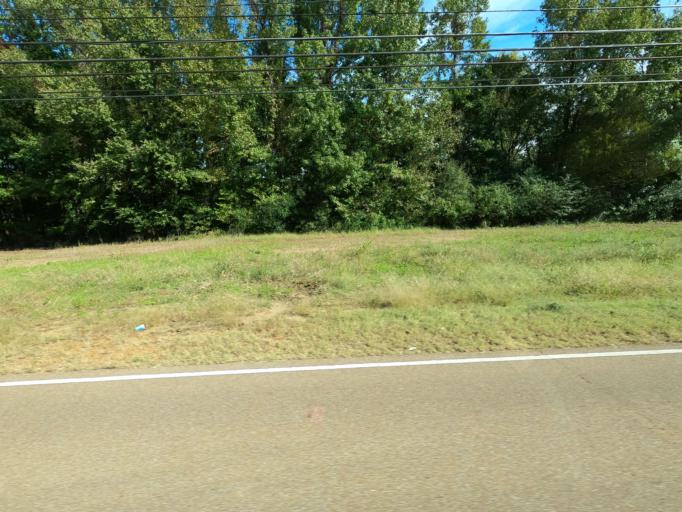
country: US
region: Tennessee
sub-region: Fayette County
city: Hickory Withe
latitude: 35.2296
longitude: -89.6500
